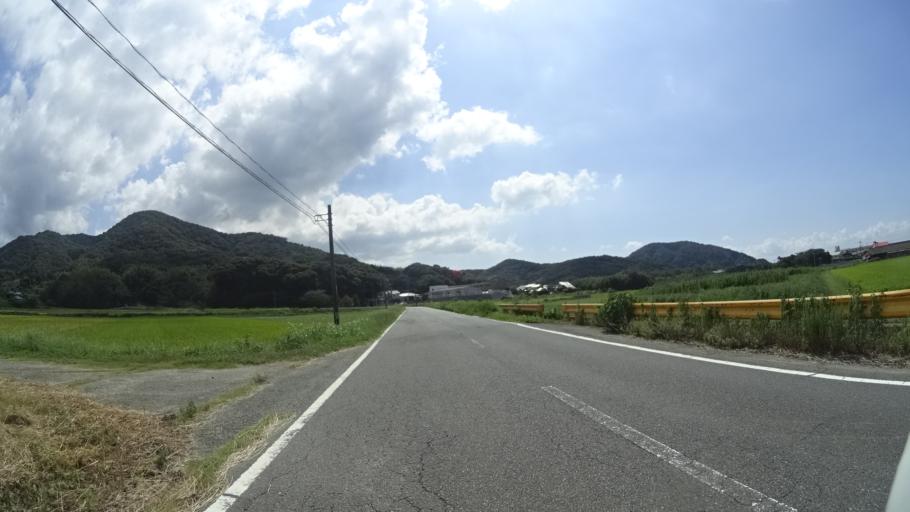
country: JP
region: Yamaguchi
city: Shimonoseki
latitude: 34.0935
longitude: 130.8805
